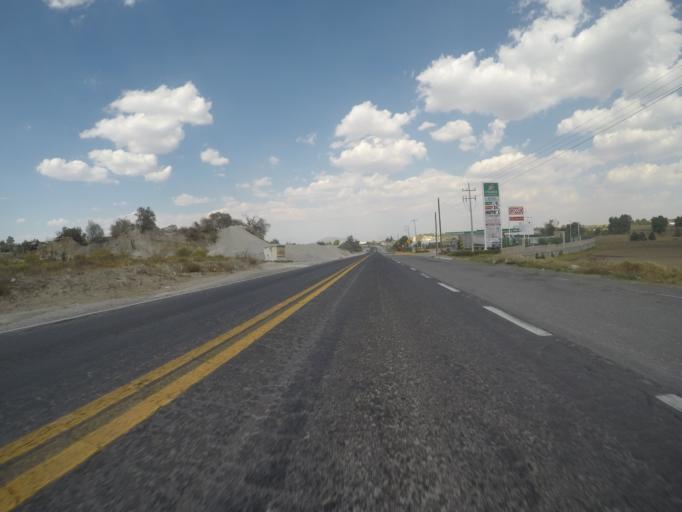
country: MX
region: Mexico
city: San Juan de las Huertas
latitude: 19.2302
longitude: -99.7818
